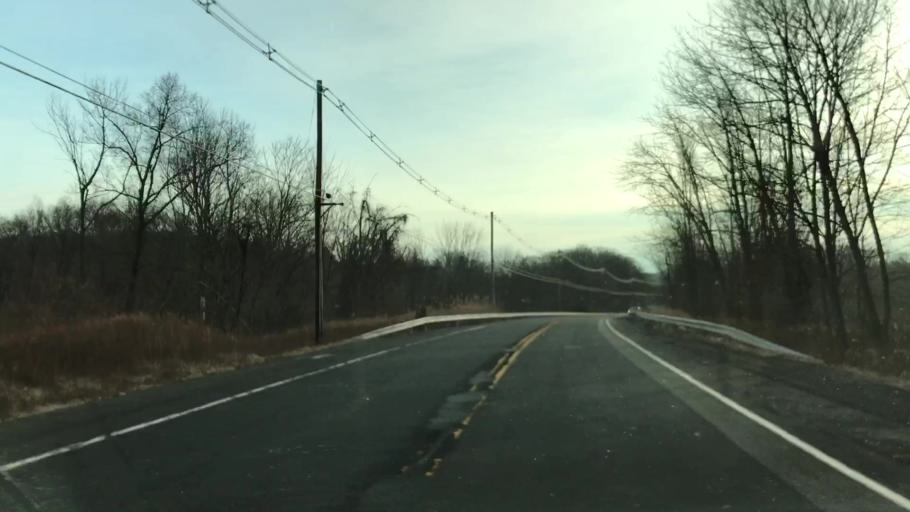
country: US
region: New York
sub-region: Rockland County
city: Pomona
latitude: 41.1835
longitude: -74.0612
